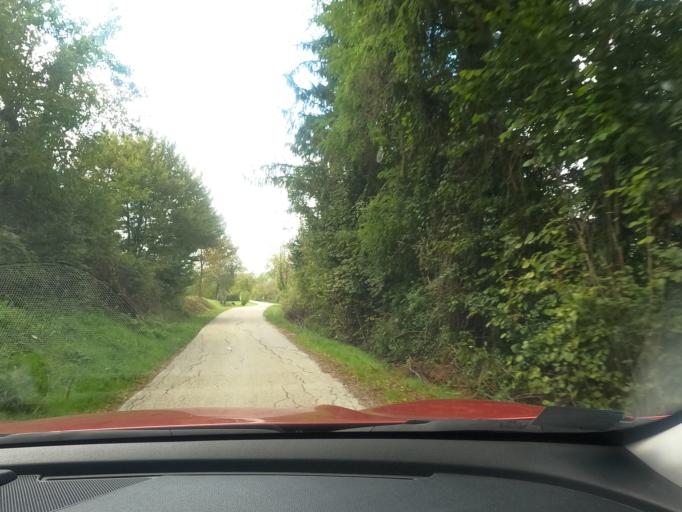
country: HR
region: Karlovacka
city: Vojnic
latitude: 45.2413
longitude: 15.7096
